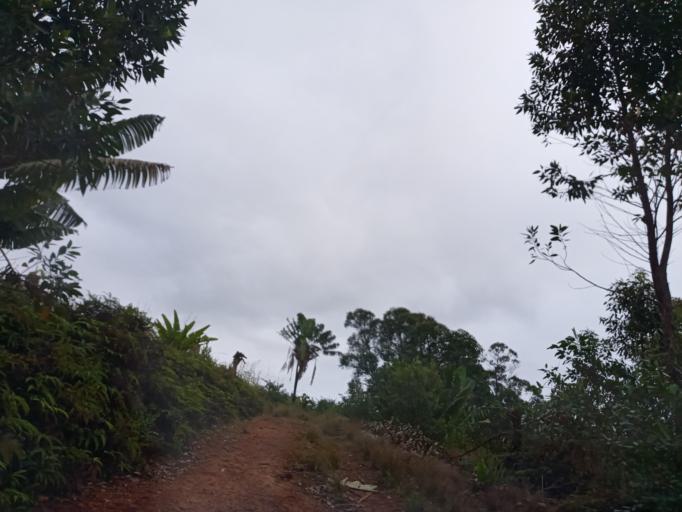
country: MG
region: Atsimo-Atsinanana
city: Vohipaho
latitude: -24.0032
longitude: 47.4048
